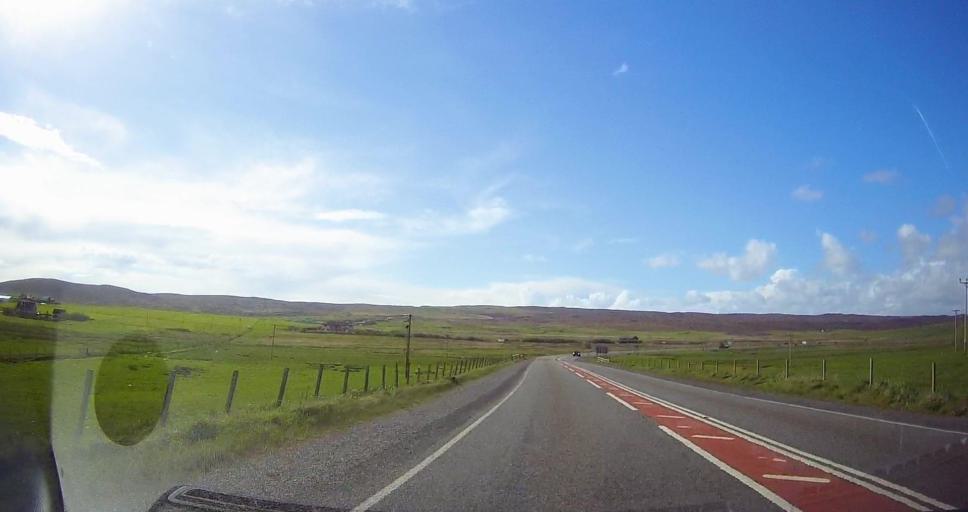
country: GB
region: Scotland
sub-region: Shetland Islands
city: Lerwick
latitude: 60.1865
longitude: -1.2267
